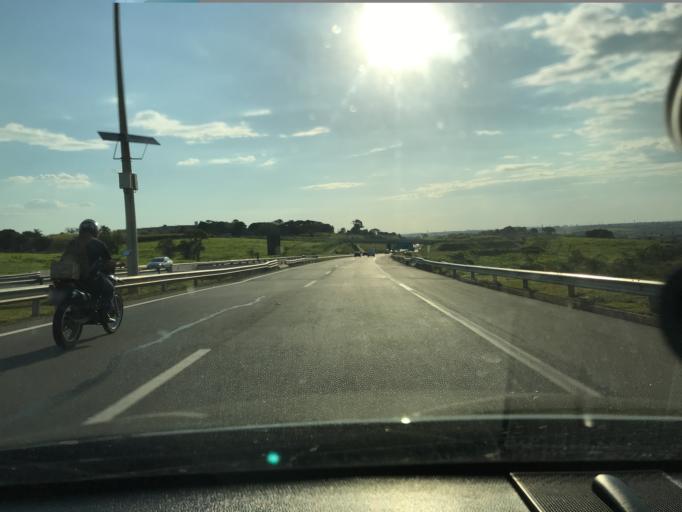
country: BR
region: Sao Paulo
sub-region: Valinhos
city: Valinhos
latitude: -22.9877
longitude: -47.0566
